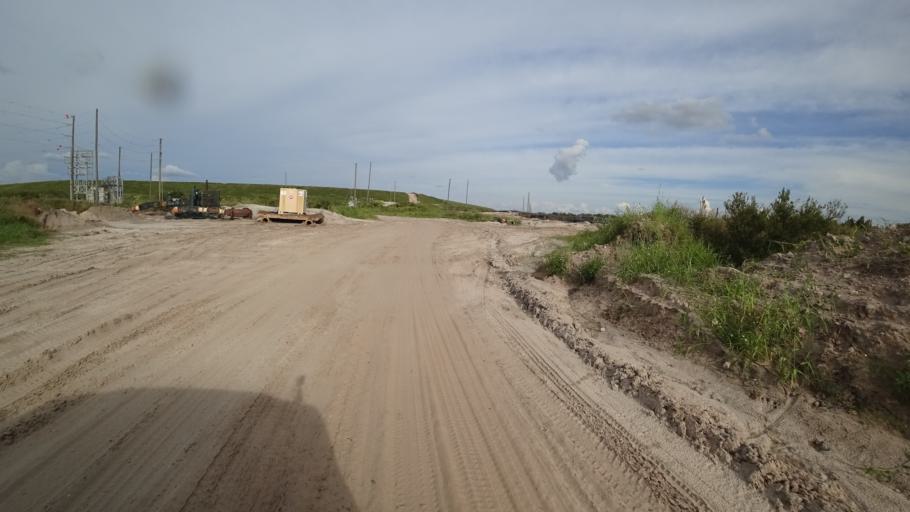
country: US
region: Florida
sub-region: Hardee County
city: Wauchula
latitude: 27.5304
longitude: -82.0698
